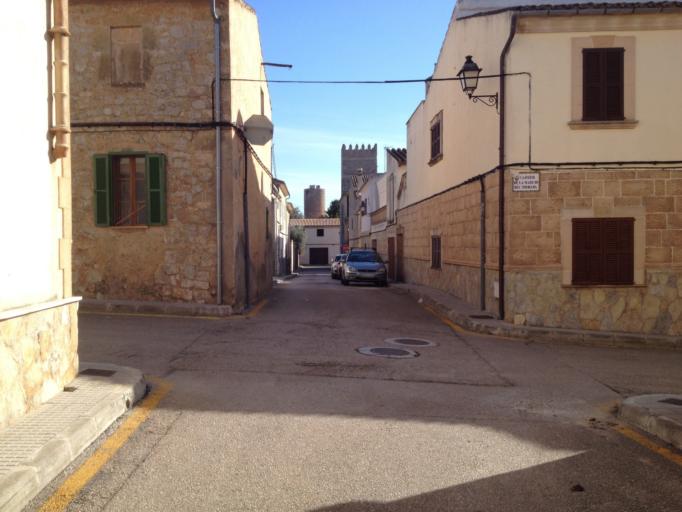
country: ES
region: Balearic Islands
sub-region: Illes Balears
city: Sant Llorenc des Cardassar
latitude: 39.6124
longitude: 3.2876
